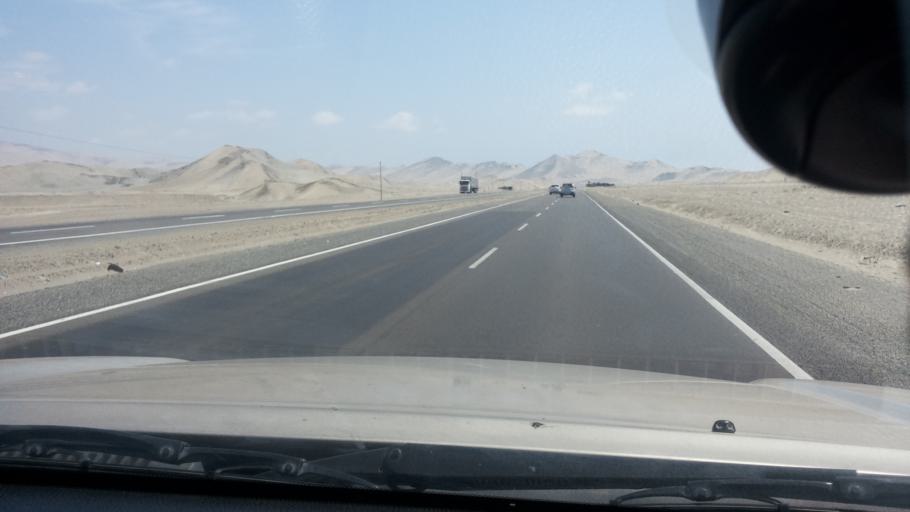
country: PE
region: Ancash
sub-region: Provincia de Casma
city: Casma
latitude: -9.6107
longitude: -78.2576
